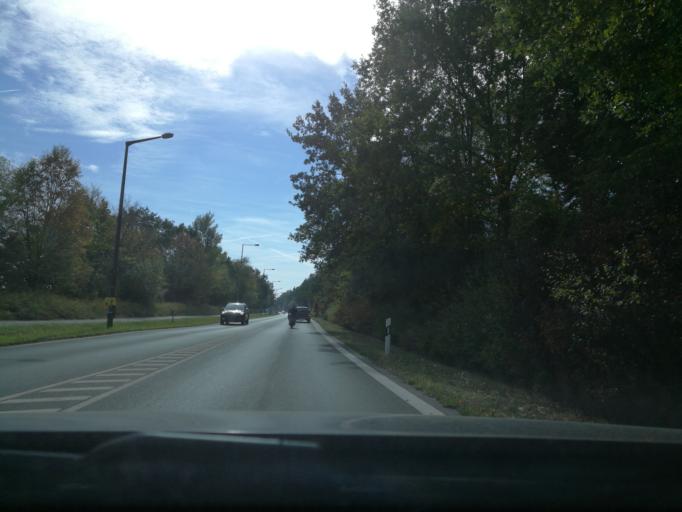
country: DE
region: Bavaria
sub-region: Regierungsbezirk Mittelfranken
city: Furth
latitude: 49.5084
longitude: 10.9652
